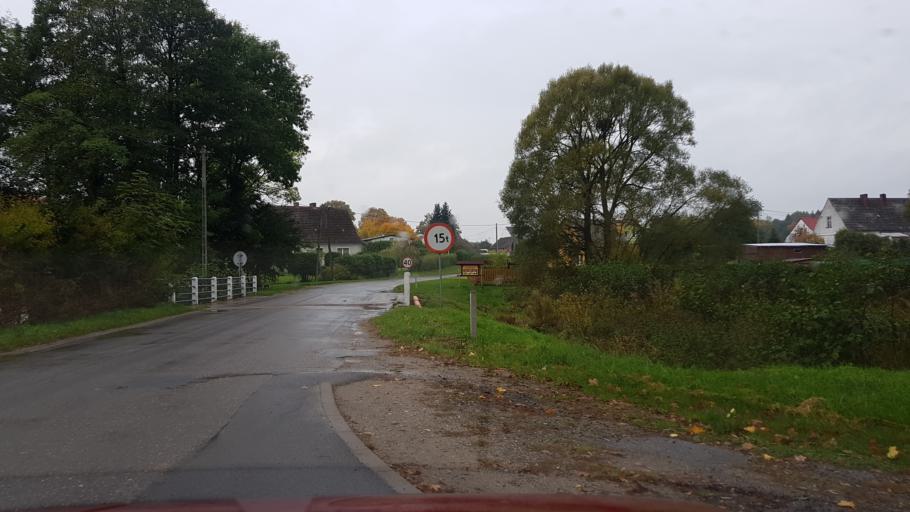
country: PL
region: West Pomeranian Voivodeship
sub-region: Powiat walecki
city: Walcz
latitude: 53.3705
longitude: 16.4293
